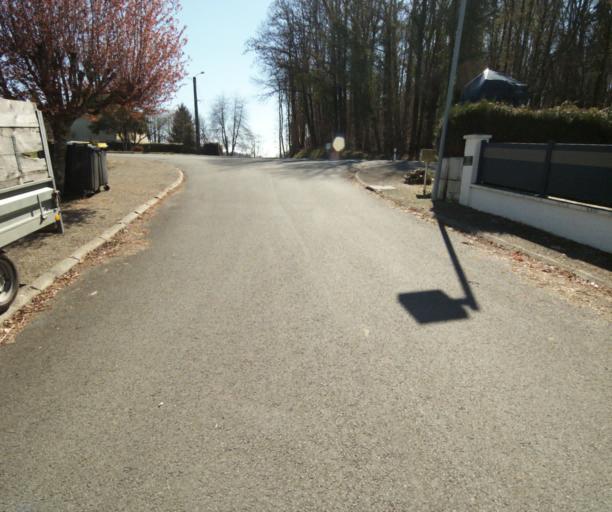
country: FR
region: Limousin
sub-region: Departement de la Correze
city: Saint-Clement
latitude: 45.3459
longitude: 1.6383
